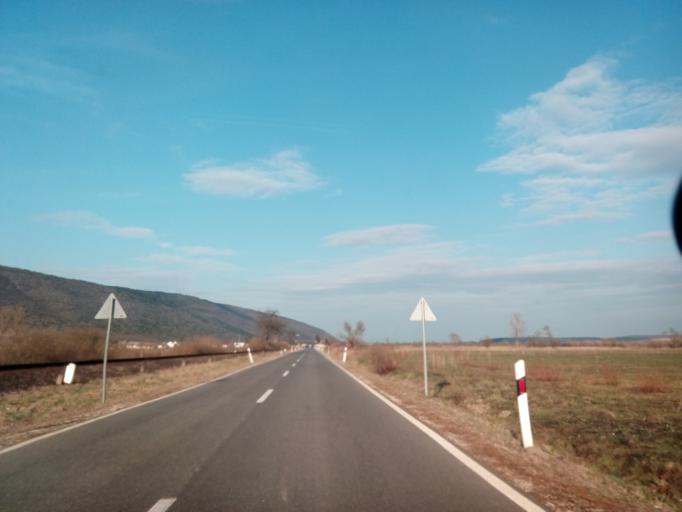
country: HU
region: Borsod-Abauj-Zemplen
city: Szendro
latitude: 48.5536
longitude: 20.7759
